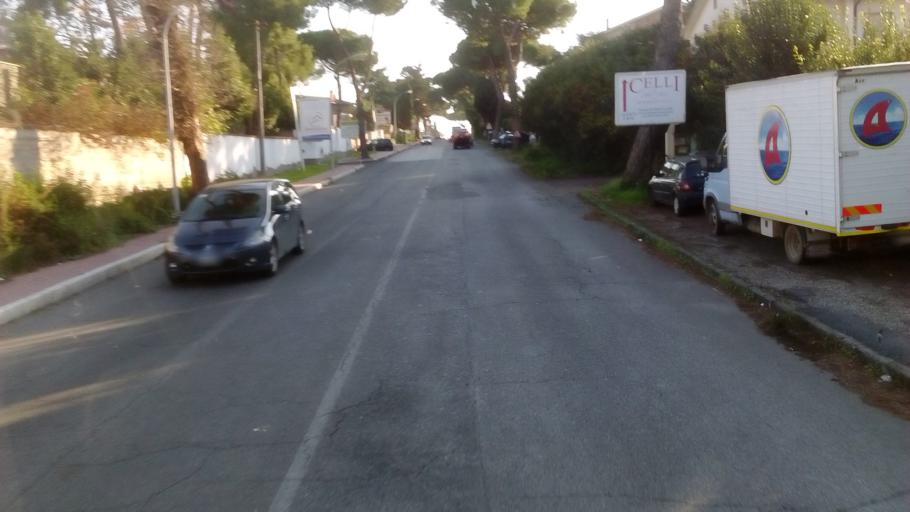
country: IT
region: Latium
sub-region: Citta metropolitana di Roma Capitale
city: Marino
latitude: 41.7631
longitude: 12.6161
